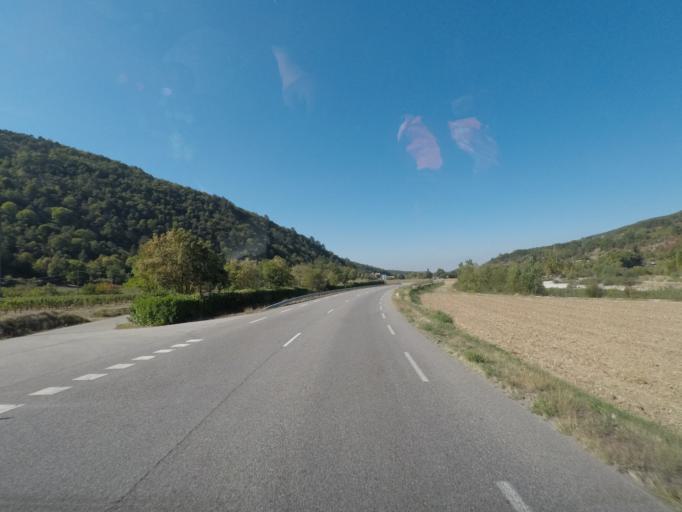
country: FR
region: Rhone-Alpes
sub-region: Departement de la Drome
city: Aouste-sur-Sye
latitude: 44.6921
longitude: 5.1831
